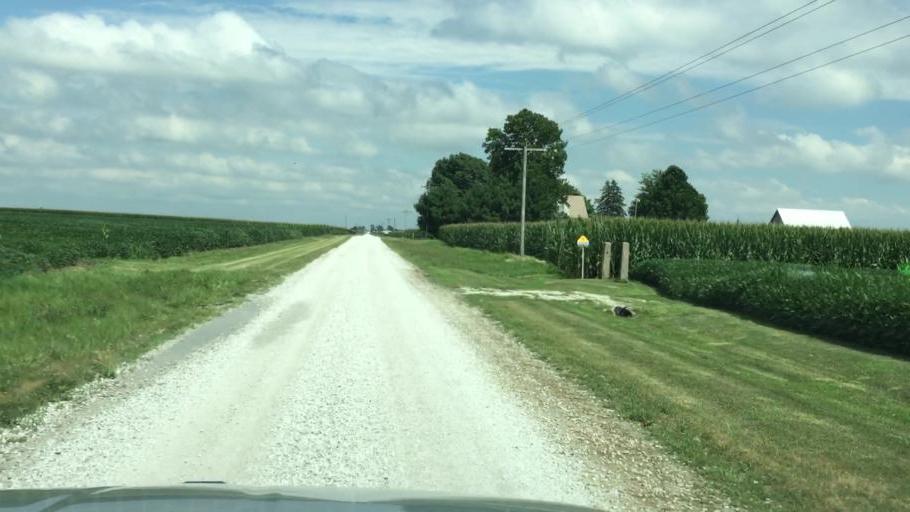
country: US
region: Illinois
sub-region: Hancock County
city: Nauvoo
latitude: 40.5216
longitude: -91.2935
